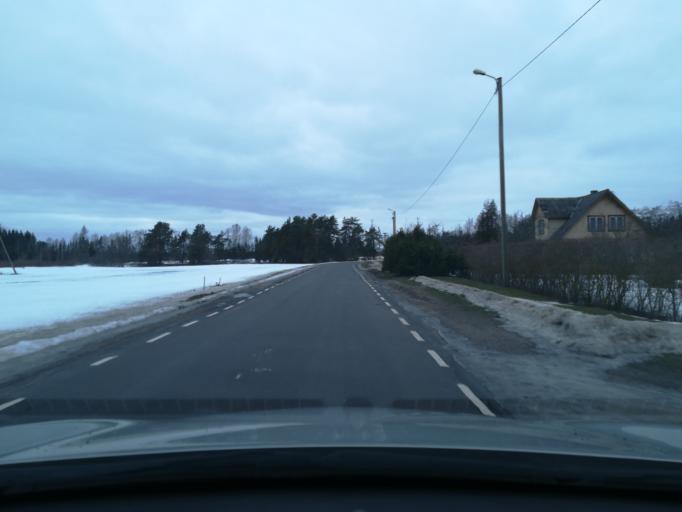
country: EE
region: Harju
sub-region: Nissi vald
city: Riisipere
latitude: 59.1117
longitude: 24.3128
